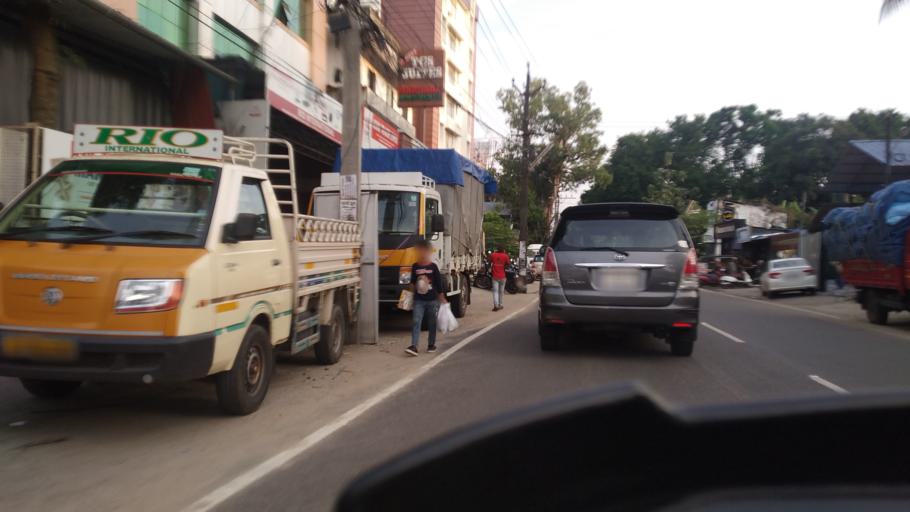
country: IN
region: Kerala
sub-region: Ernakulam
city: Elur
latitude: 10.0309
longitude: 76.3040
